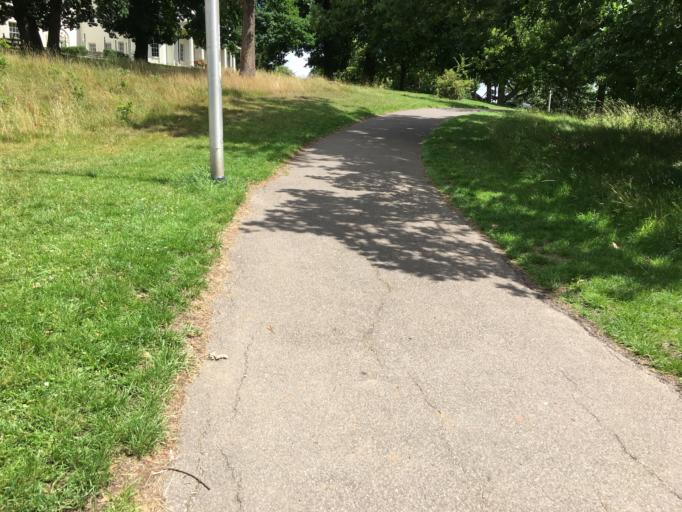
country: GB
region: England
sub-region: West Berkshire
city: Tilehurst
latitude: 51.4489
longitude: -1.0122
